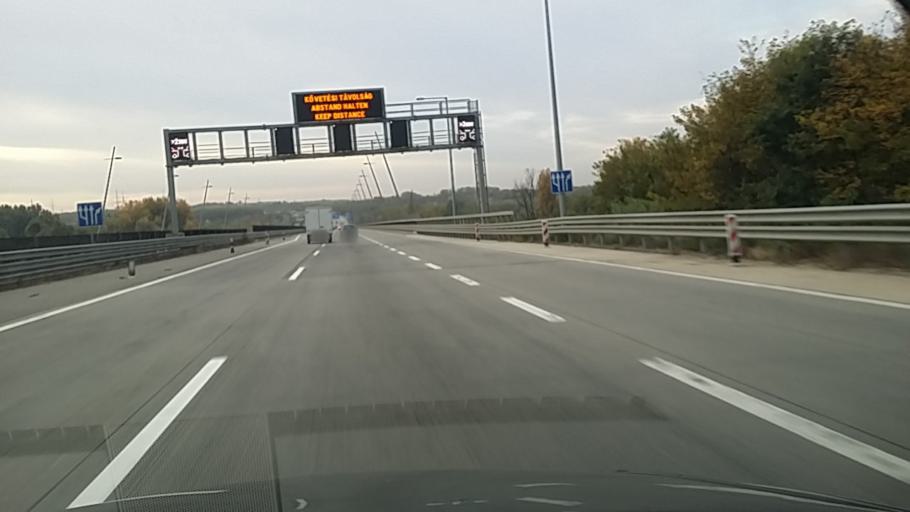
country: HU
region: Pest
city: Pecel
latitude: 47.4975
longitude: 19.3093
